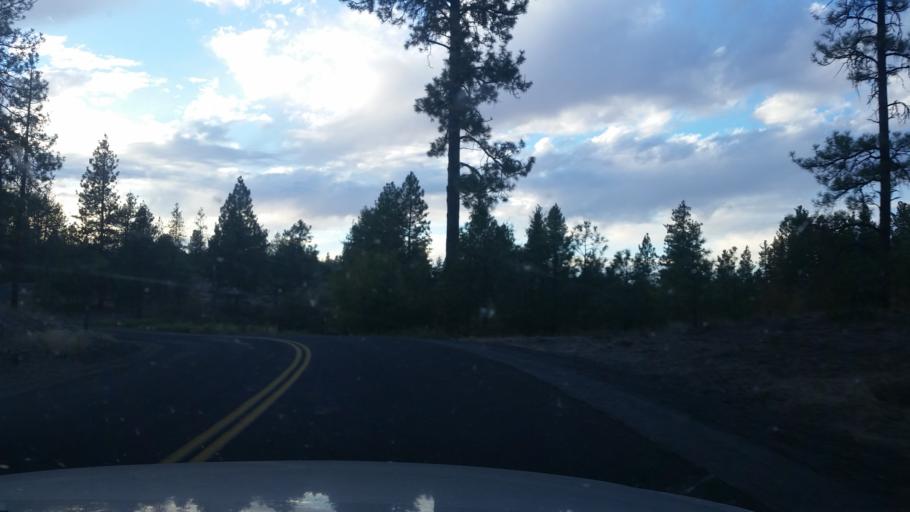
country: US
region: Washington
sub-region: Spokane County
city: Medical Lake
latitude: 47.5430
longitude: -117.6902
